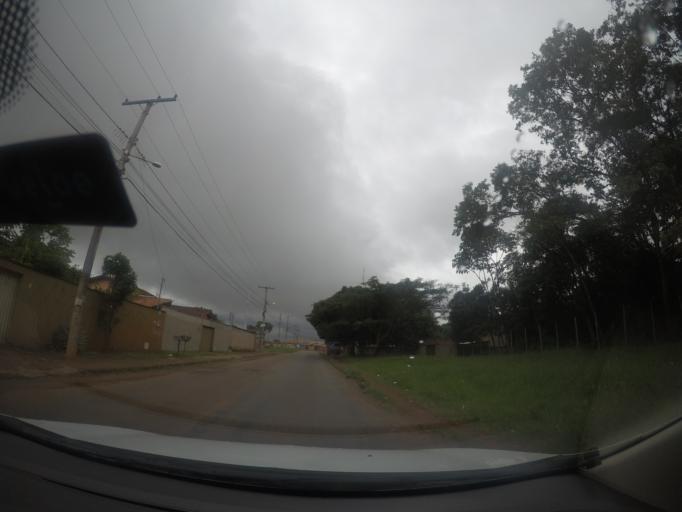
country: BR
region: Goias
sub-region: Trindade
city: Trindade
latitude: -16.6144
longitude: -49.3917
